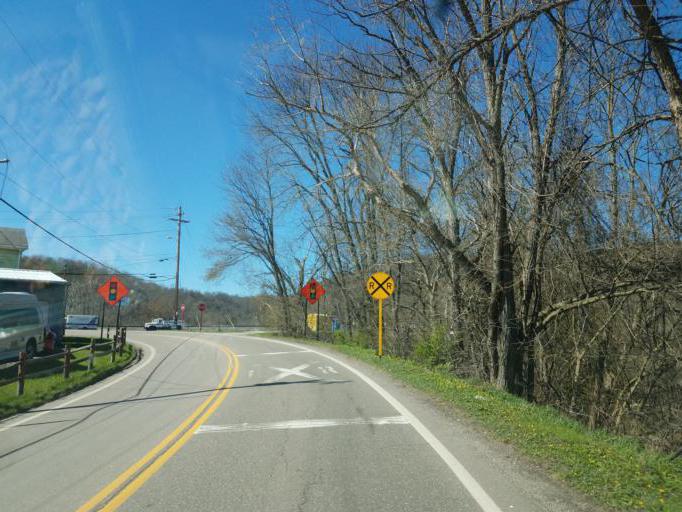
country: US
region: Ohio
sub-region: Jefferson County
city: Tiltonsville
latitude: 40.1873
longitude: -80.6885
